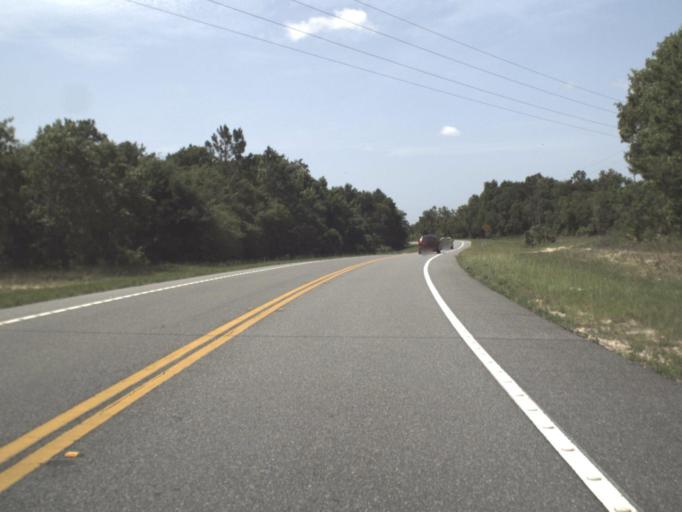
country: US
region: Florida
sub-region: Taylor County
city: Steinhatchee
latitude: 29.7104
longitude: -83.3583
